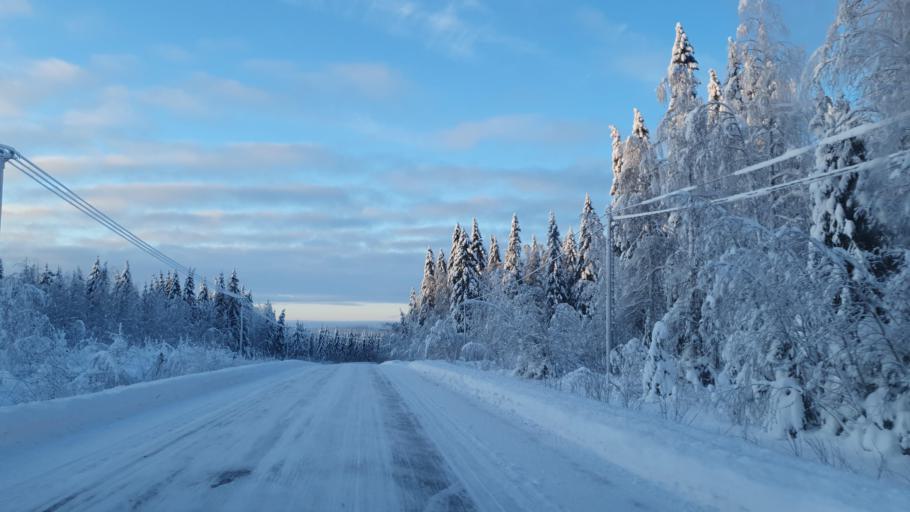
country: FI
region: Kainuu
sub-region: Kajaani
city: Ristijaervi
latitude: 64.3374
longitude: 28.0668
